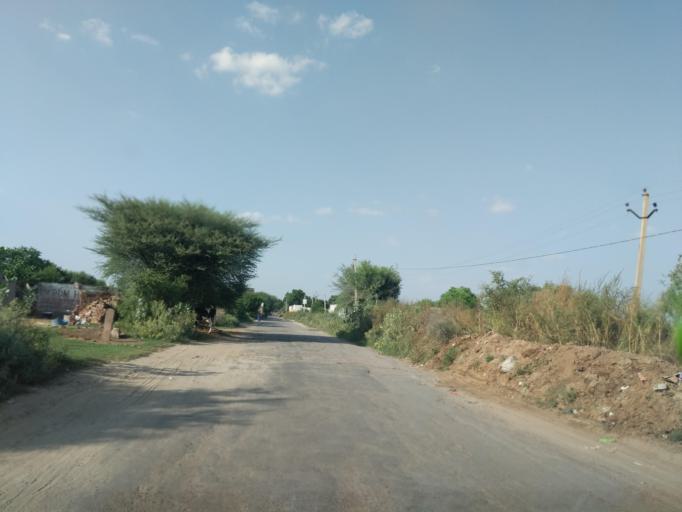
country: IN
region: Rajasthan
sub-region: Churu
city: Rajgarh
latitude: 28.5289
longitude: 75.3775
